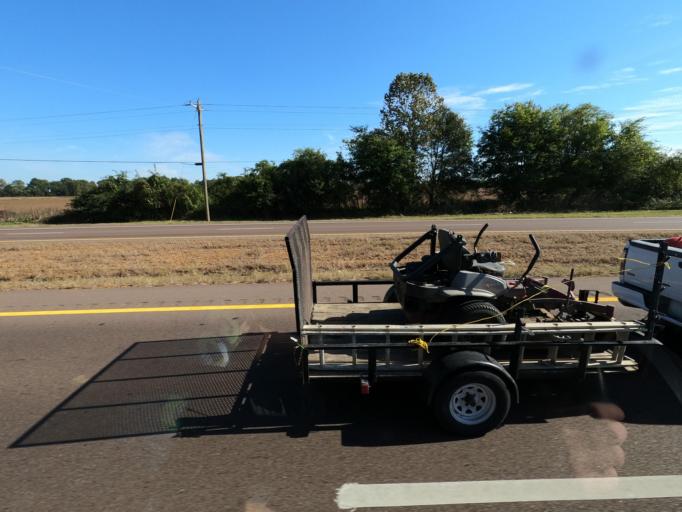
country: US
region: Tennessee
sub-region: Obion County
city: Union City
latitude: 36.3927
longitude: -89.0991
